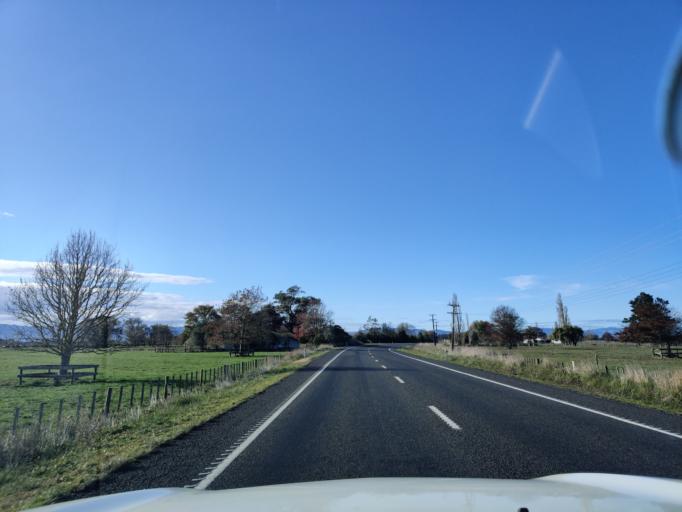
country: NZ
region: Waikato
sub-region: Hauraki District
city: Ngatea
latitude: -37.2834
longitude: 175.5432
